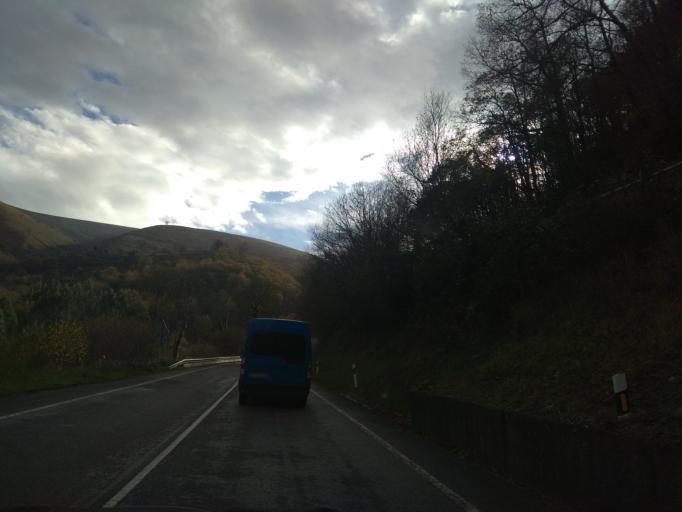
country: ES
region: Cantabria
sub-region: Provincia de Cantabria
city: San Pedro del Romeral
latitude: 43.1455
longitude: -3.8997
